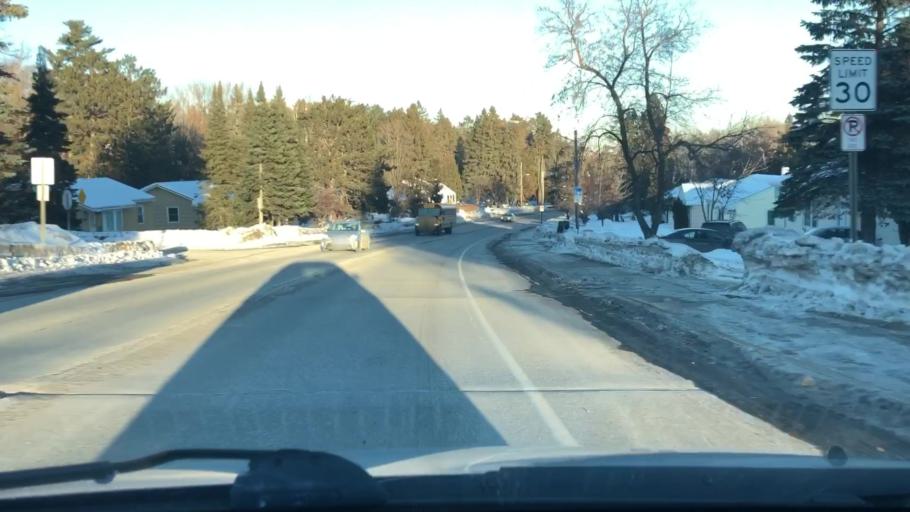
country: US
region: Minnesota
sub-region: Saint Louis County
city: Duluth
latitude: 46.8247
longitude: -92.0918
